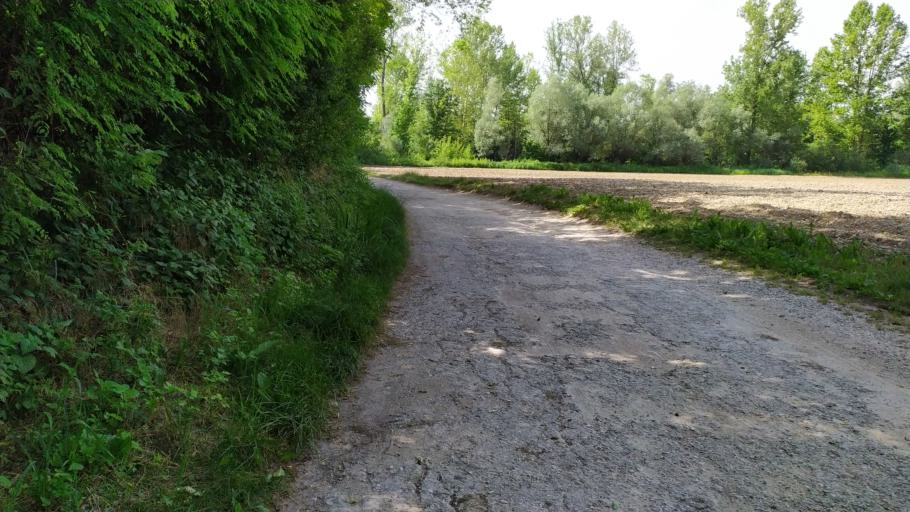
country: IT
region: Veneto
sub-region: Provincia di Treviso
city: Sernaglia della Battaglia
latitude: 45.8605
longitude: 12.1414
